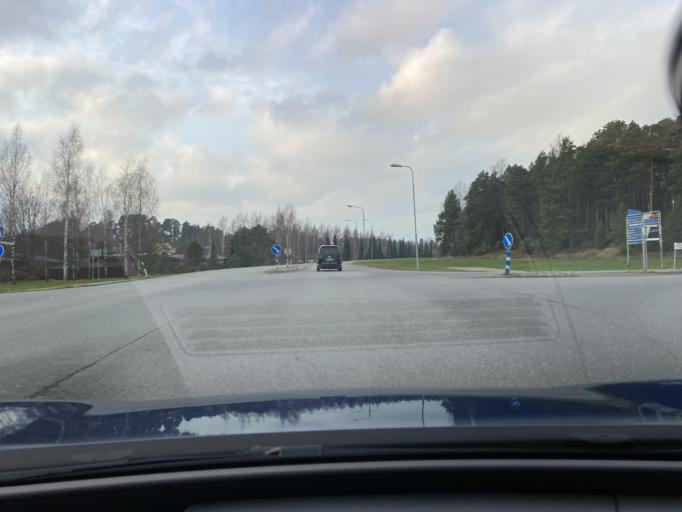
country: FI
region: Varsinais-Suomi
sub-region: Turku
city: Naantali
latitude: 60.4752
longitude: 22.0484
